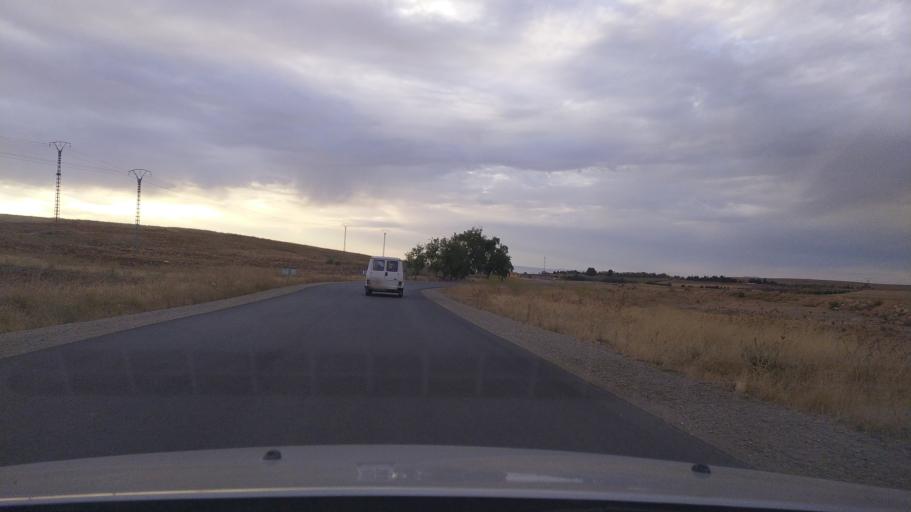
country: DZ
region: Tiaret
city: Frenda
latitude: 35.0139
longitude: 1.1137
